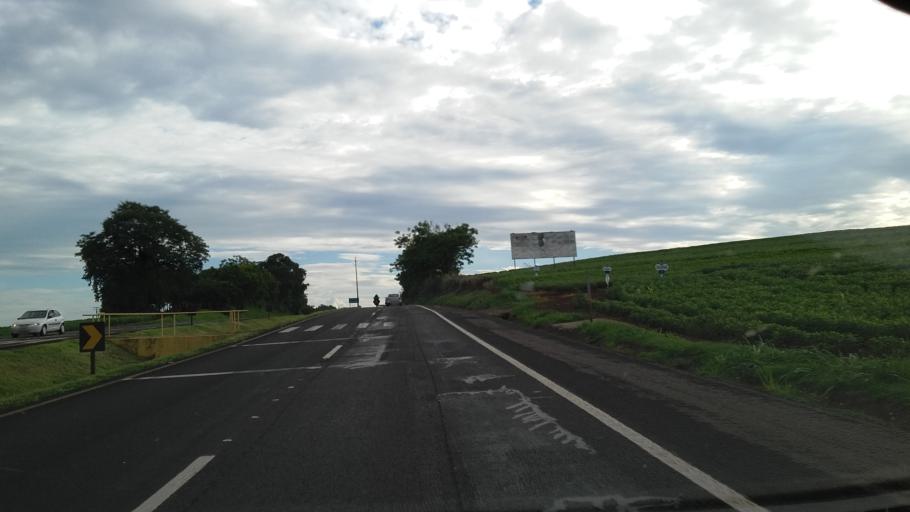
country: BR
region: Parana
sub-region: Paicandu
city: Paicandu
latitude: -23.5144
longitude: -52.0265
